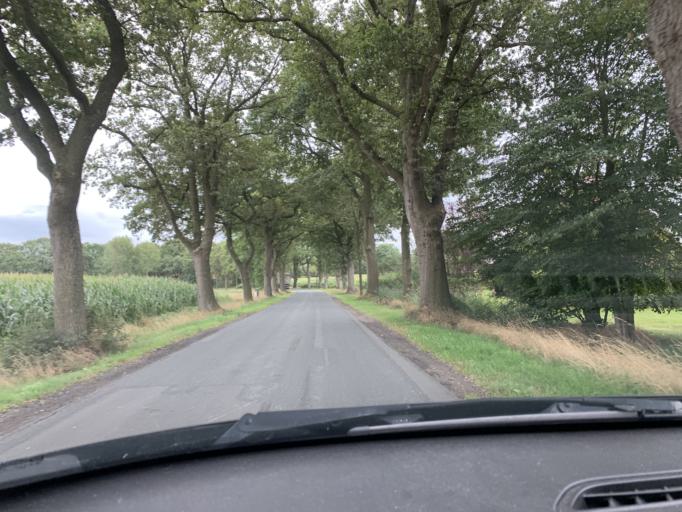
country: DE
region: Lower Saxony
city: Westerstede
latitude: 53.2764
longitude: 7.8898
